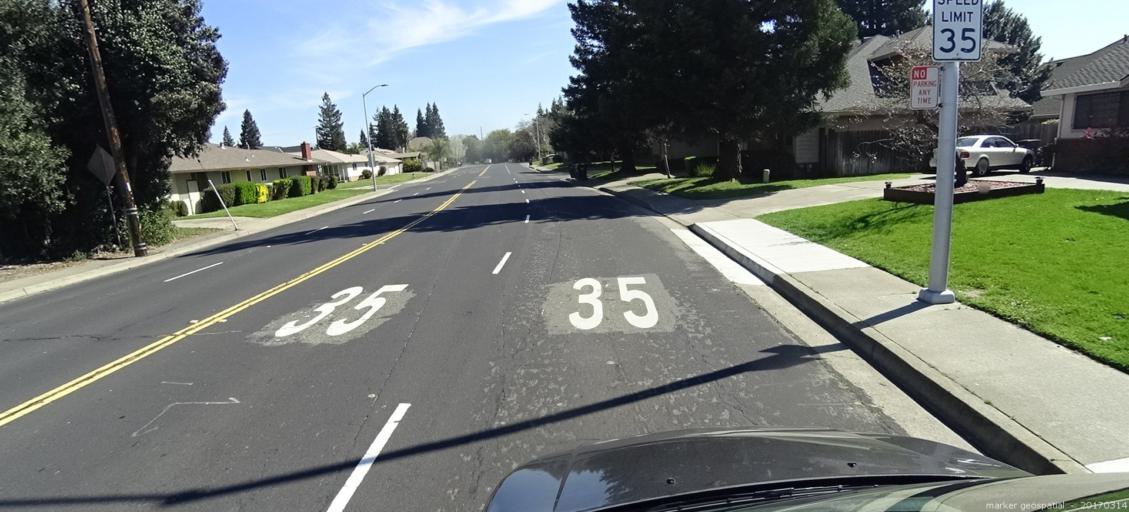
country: US
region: California
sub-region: Yolo County
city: West Sacramento
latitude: 38.5248
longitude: -121.5166
